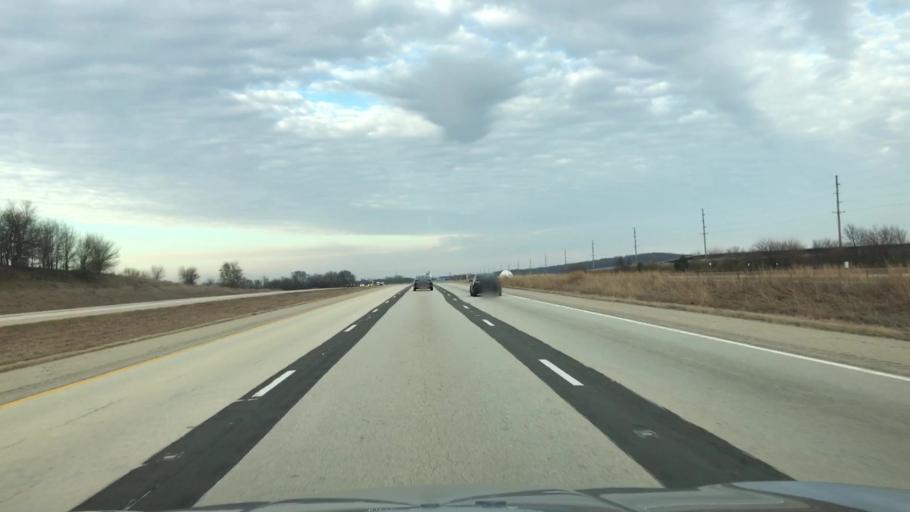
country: US
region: Illinois
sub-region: Sangamon County
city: Williamsville
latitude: 39.9940
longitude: -89.5110
